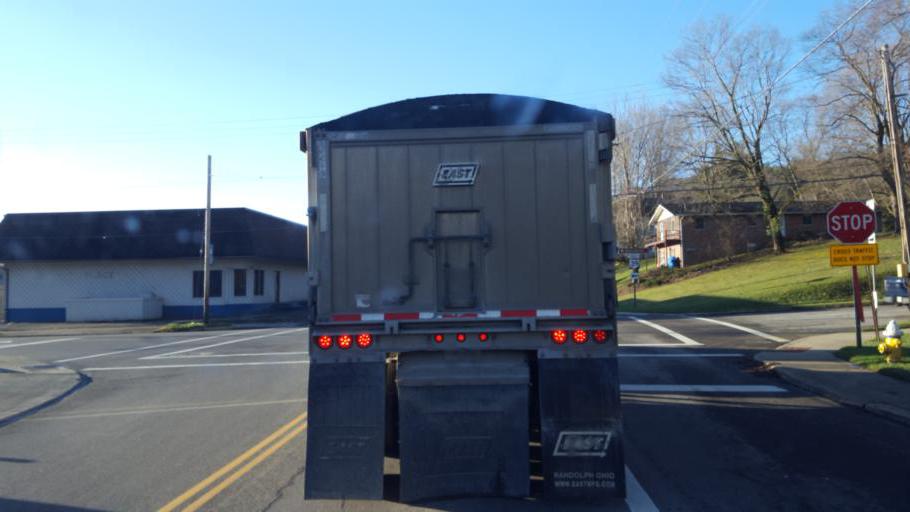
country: US
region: Ohio
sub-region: Ashland County
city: Loudonville
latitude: 40.6360
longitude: -82.2408
